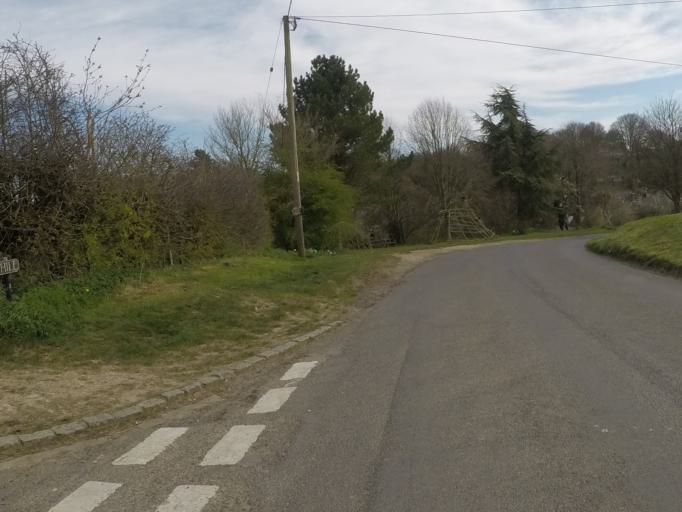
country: GB
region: England
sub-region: Oxfordshire
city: Charlbury
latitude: 51.8441
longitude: -1.4766
